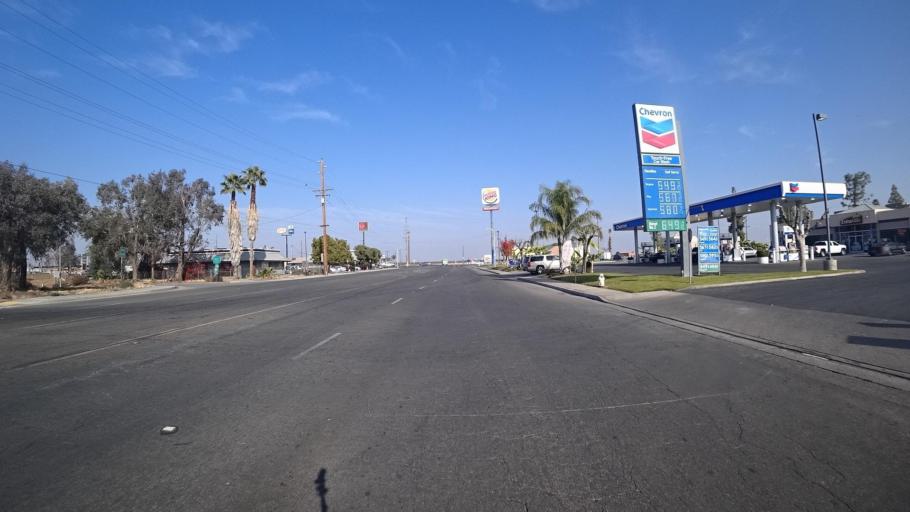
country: US
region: California
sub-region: Kern County
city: Delano
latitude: 35.7891
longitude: -119.2492
